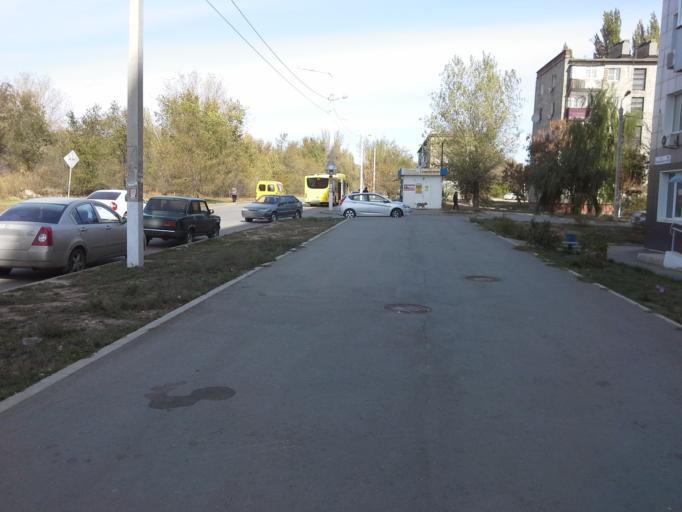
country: RU
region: Volgograd
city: Vodstroy
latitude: 48.8386
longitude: 44.6375
